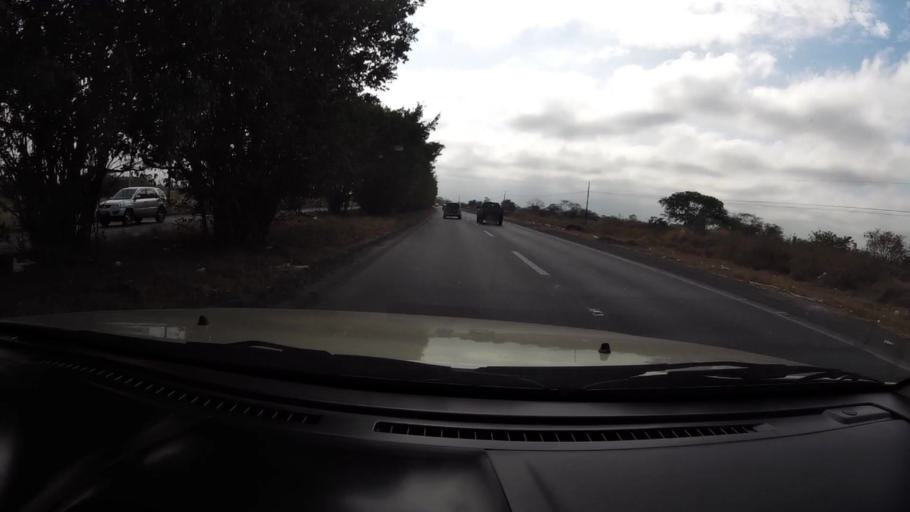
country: EC
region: Guayas
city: Eloy Alfaro
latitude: -2.1985
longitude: -79.7796
